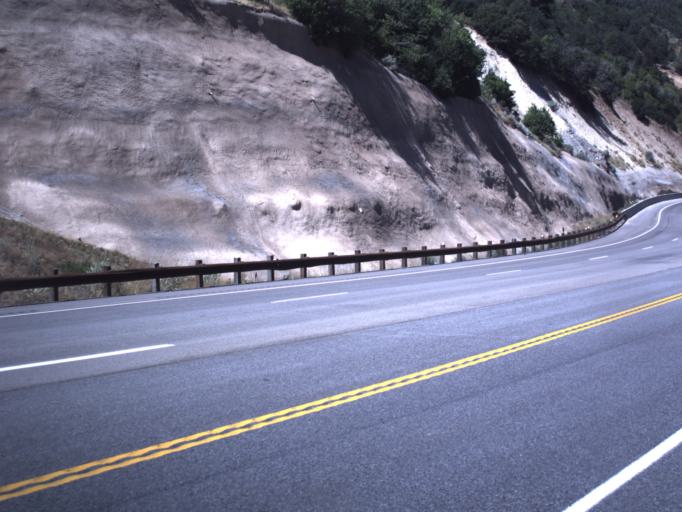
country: US
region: Utah
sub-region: Wasatch County
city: Midway
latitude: 40.3818
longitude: -111.5513
